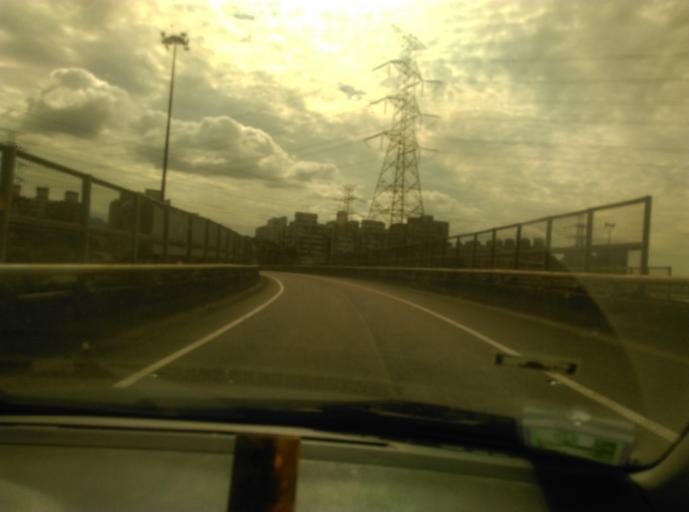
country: TW
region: Taiwan
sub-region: Keelung
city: Keelung
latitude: 25.0727
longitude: 121.6438
